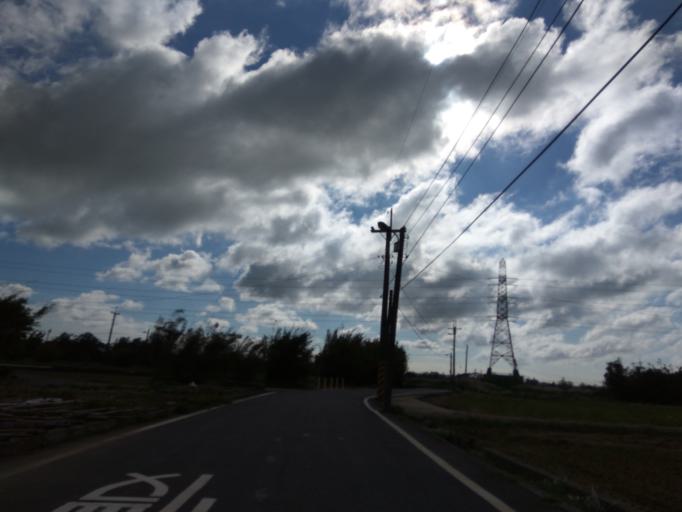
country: TW
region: Taiwan
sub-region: Hsinchu
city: Zhubei
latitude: 24.9712
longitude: 121.0789
